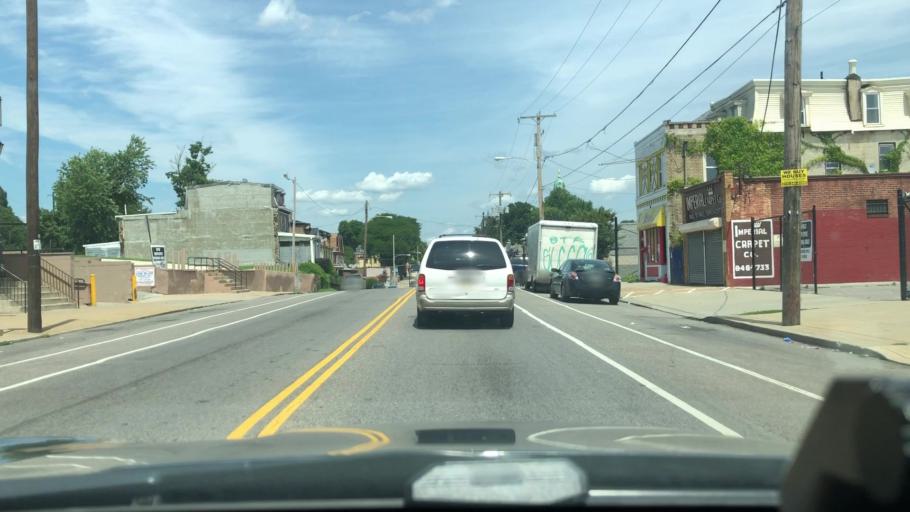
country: US
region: Pennsylvania
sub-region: Montgomery County
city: Wyndmoor
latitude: 40.0394
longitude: -75.1710
